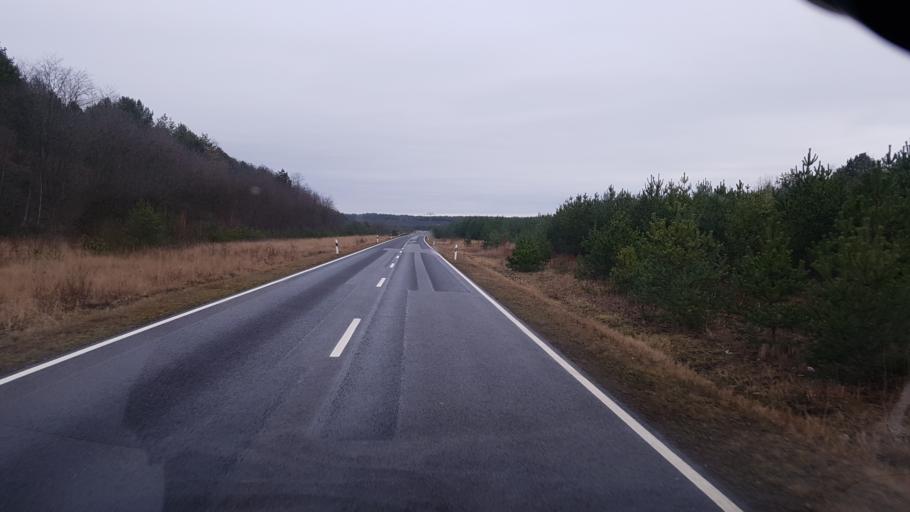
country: DE
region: Brandenburg
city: Schipkau
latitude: 51.5089
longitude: 13.8535
